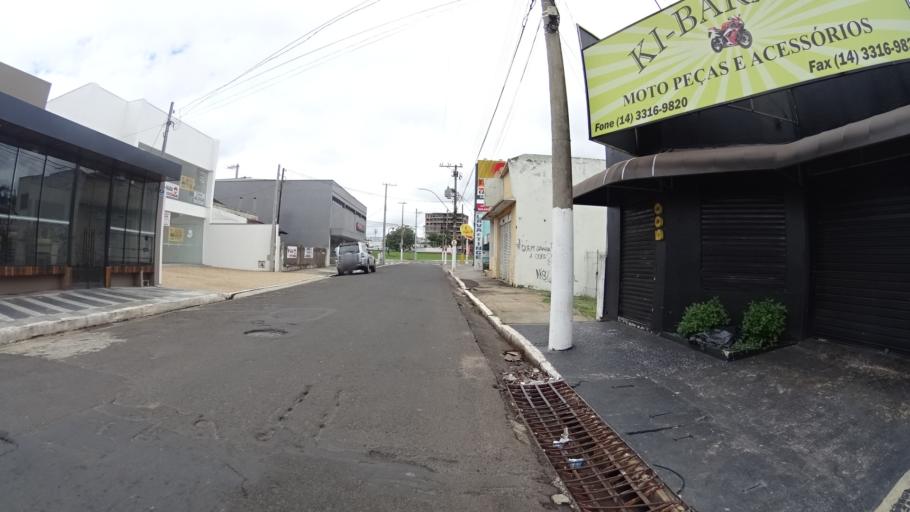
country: BR
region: Sao Paulo
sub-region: Marilia
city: Marilia
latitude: -22.2202
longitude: -49.9430
